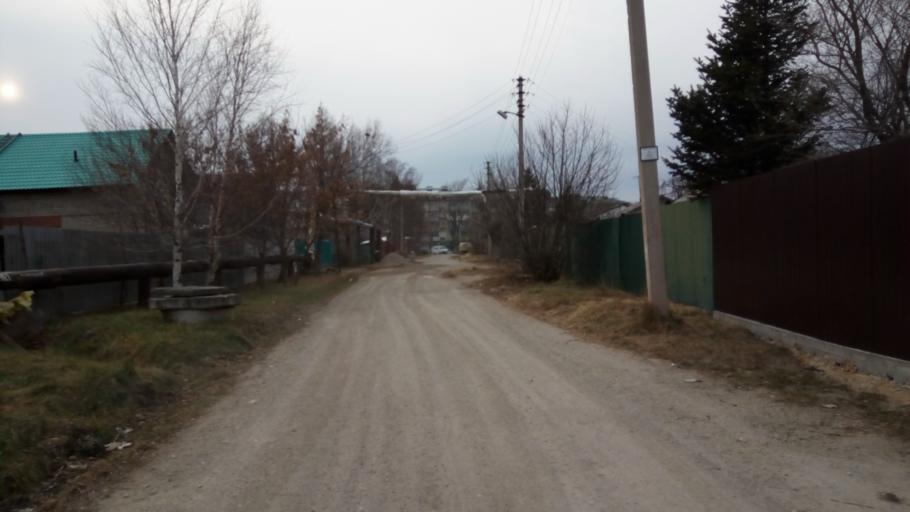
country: RU
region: Primorskiy
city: Novoshakhtinskiy
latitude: 44.0280
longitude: 132.1749
